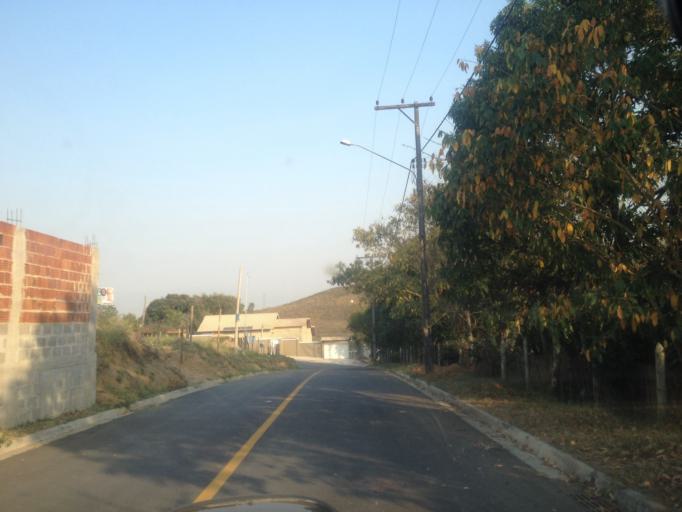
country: BR
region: Rio de Janeiro
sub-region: Porto Real
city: Porto Real
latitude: -22.4370
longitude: -44.3226
